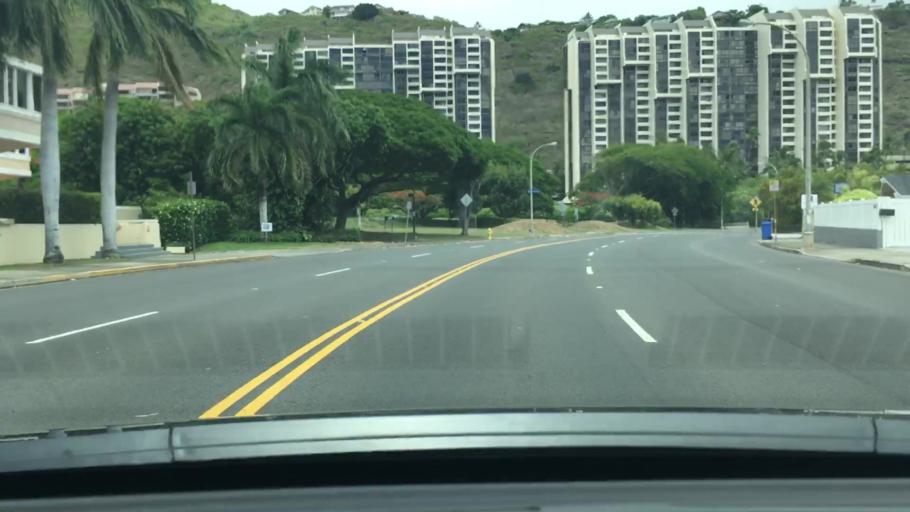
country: US
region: Hawaii
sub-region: Honolulu County
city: Waimanalo Beach
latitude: 21.2937
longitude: -157.7101
